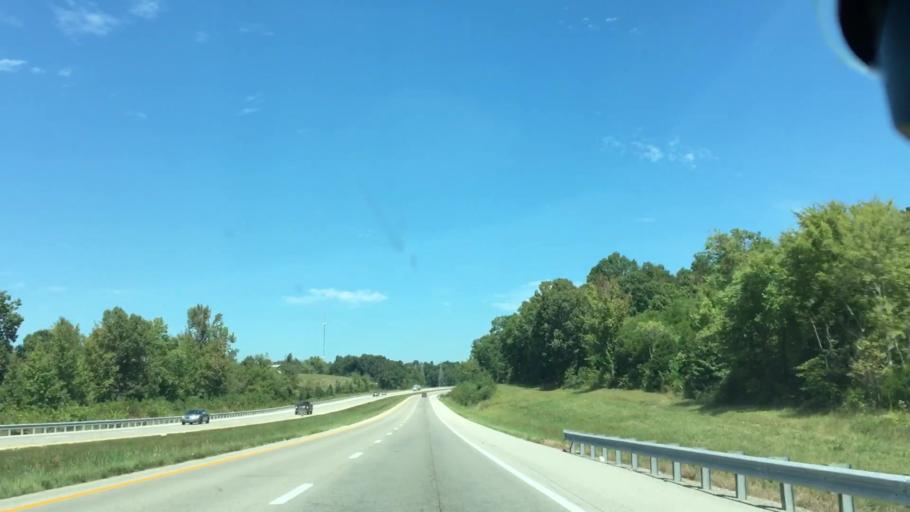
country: US
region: Kentucky
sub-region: Christian County
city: Hopkinsville
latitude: 36.9127
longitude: -87.4741
